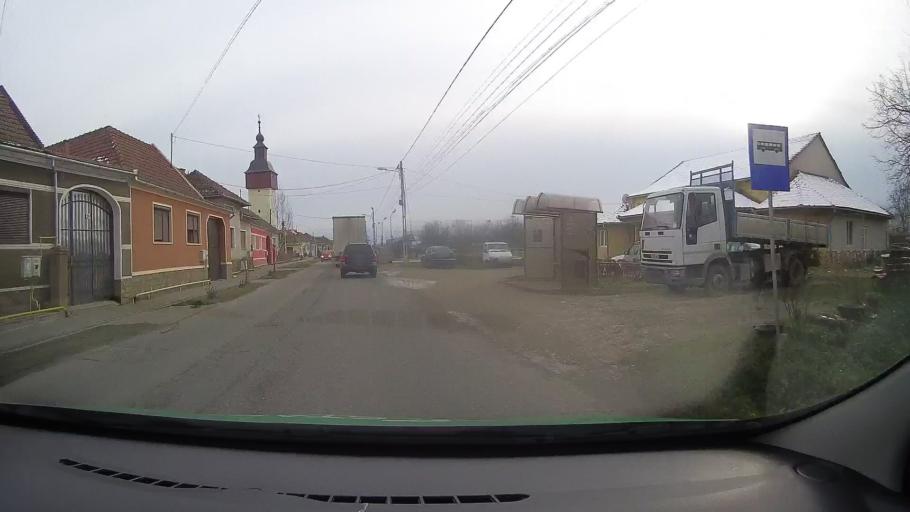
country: RO
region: Hunedoara
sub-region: Comuna Geoagiu
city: Geoagiu
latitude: 45.9017
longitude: 23.2236
